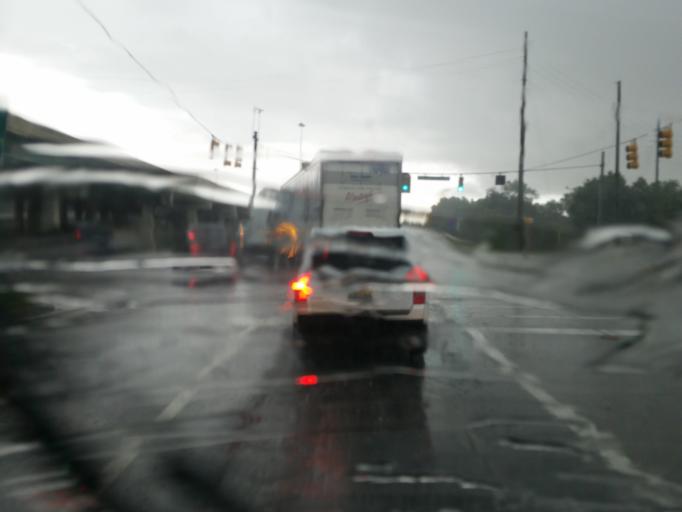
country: US
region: Alabama
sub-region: Mobile County
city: Prichard
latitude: 30.7278
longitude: -88.0734
